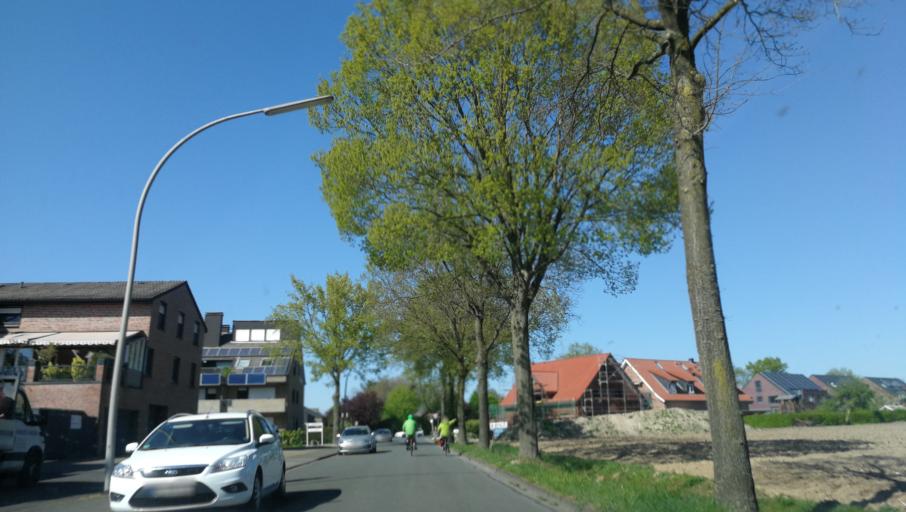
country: DE
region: North Rhine-Westphalia
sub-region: Regierungsbezirk Munster
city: Muenster
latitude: 51.9465
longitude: 7.5378
